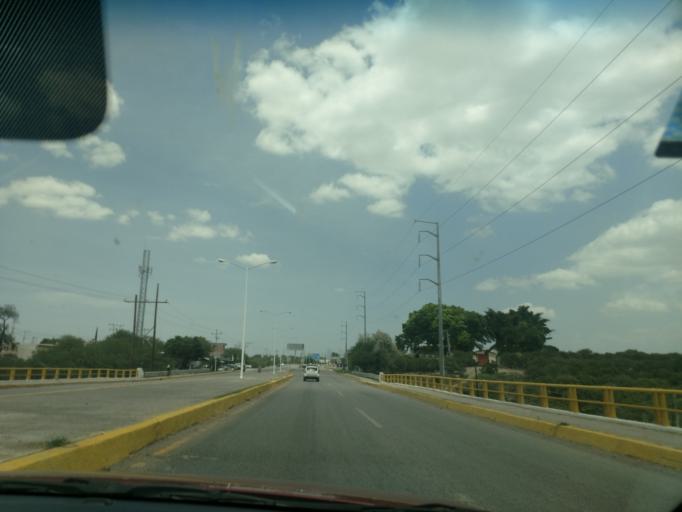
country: MX
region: San Luis Potosi
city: Rio Verde
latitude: 21.9217
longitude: -99.9656
